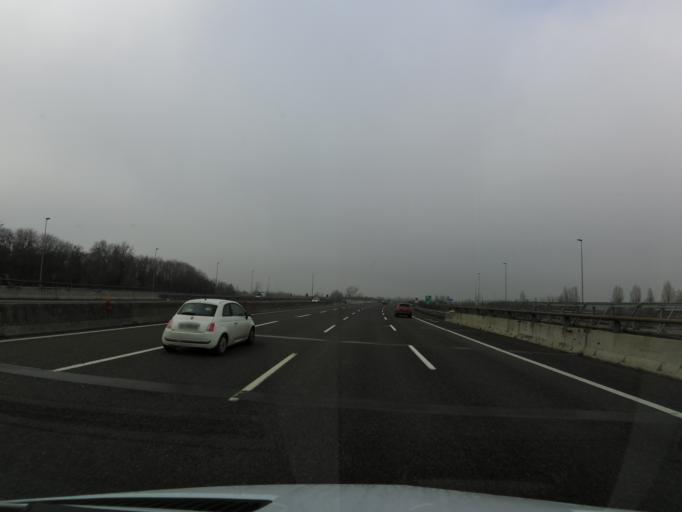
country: IT
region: Emilia-Romagna
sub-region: Provincia di Modena
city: Baggiovara
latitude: 44.6167
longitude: 10.8893
